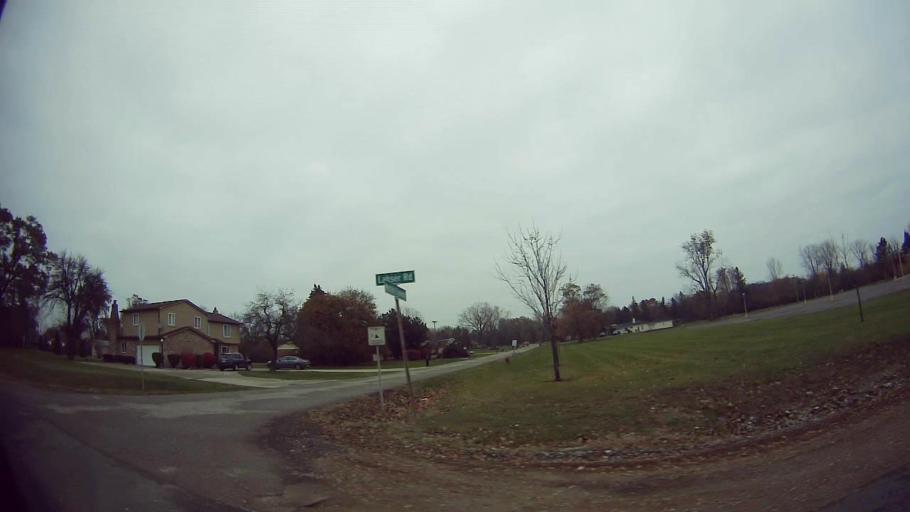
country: US
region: Michigan
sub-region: Oakland County
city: Bingham Farms
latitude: 42.5061
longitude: -83.2621
